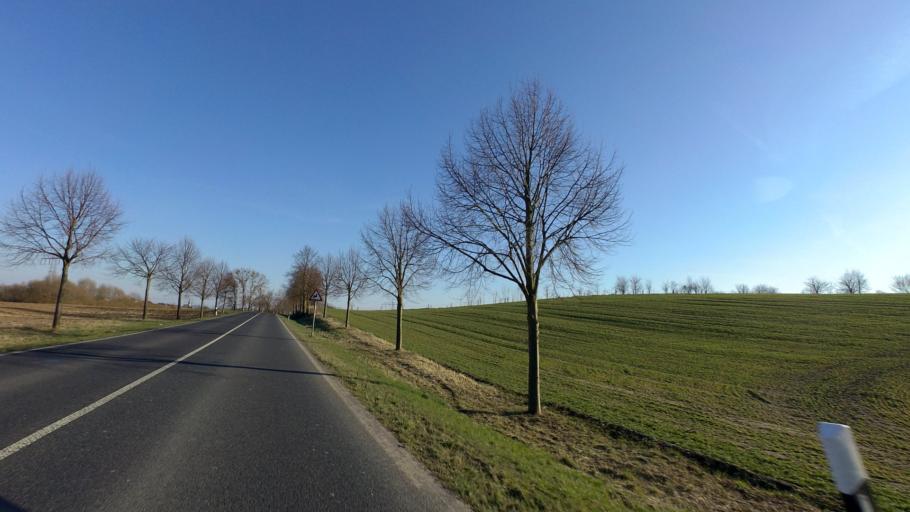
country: DE
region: Brandenburg
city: Britz
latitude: 52.9235
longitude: 13.7958
